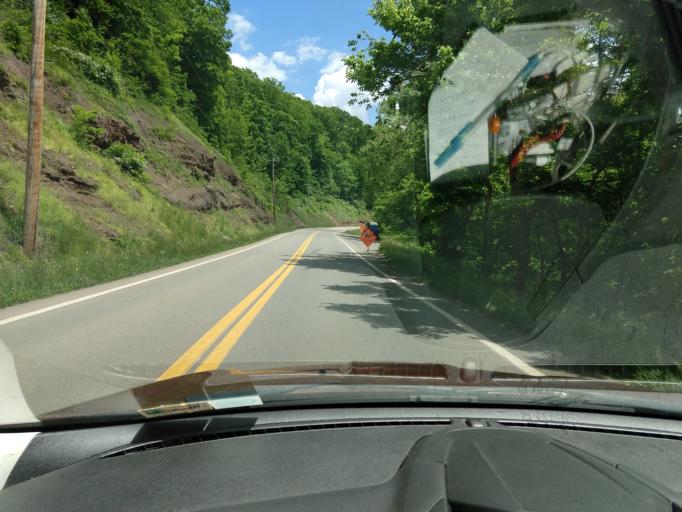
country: US
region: West Virginia
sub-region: Gilmer County
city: Glenville
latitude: 38.8890
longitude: -80.7278
